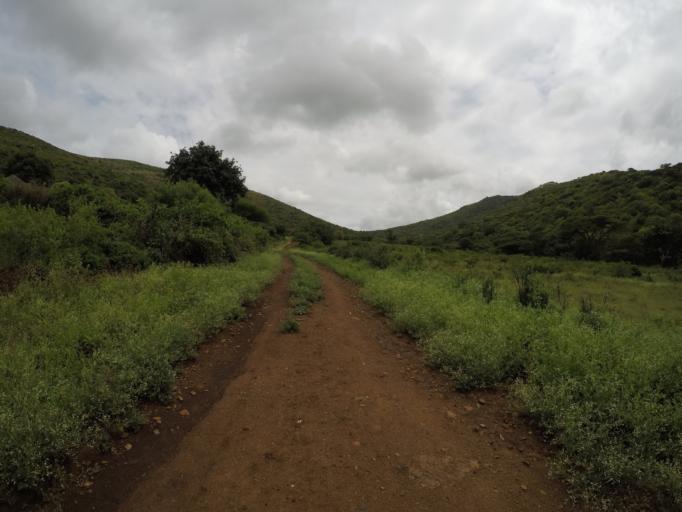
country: ZA
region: KwaZulu-Natal
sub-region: uThungulu District Municipality
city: Empangeni
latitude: -28.5828
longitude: 31.8868
